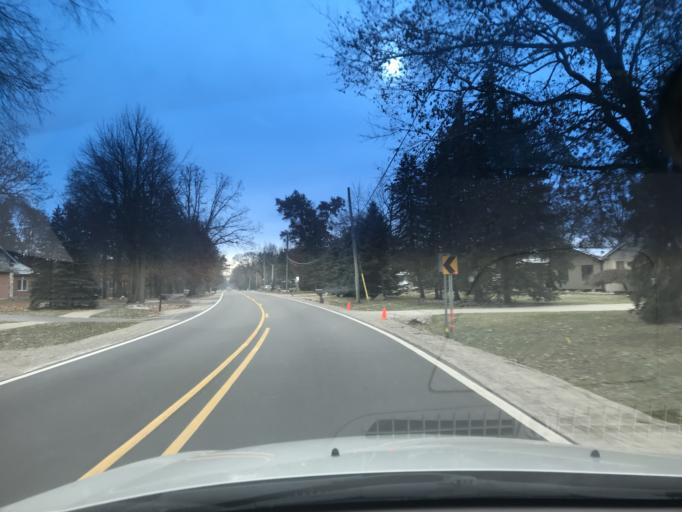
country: US
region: Michigan
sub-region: Macomb County
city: Shelby
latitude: 42.6675
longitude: -83.0631
